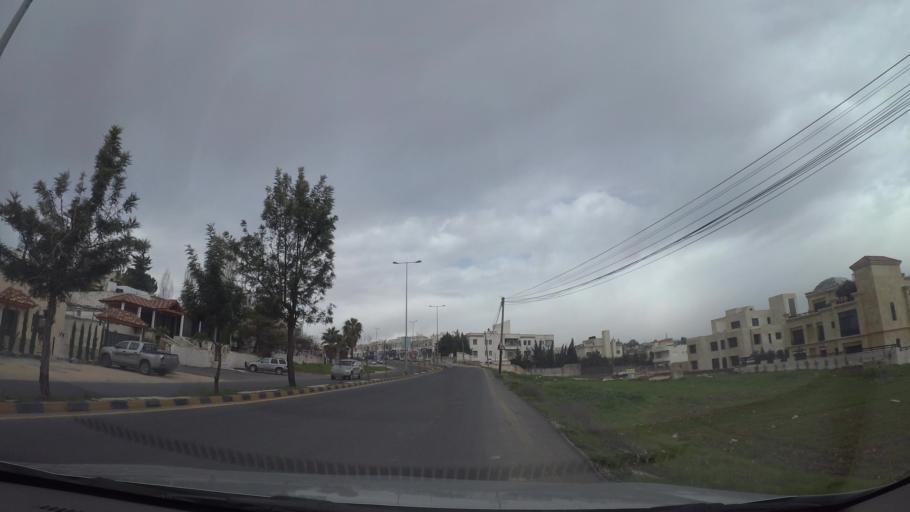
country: JO
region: Amman
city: Wadi as Sir
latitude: 31.9924
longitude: 35.8159
